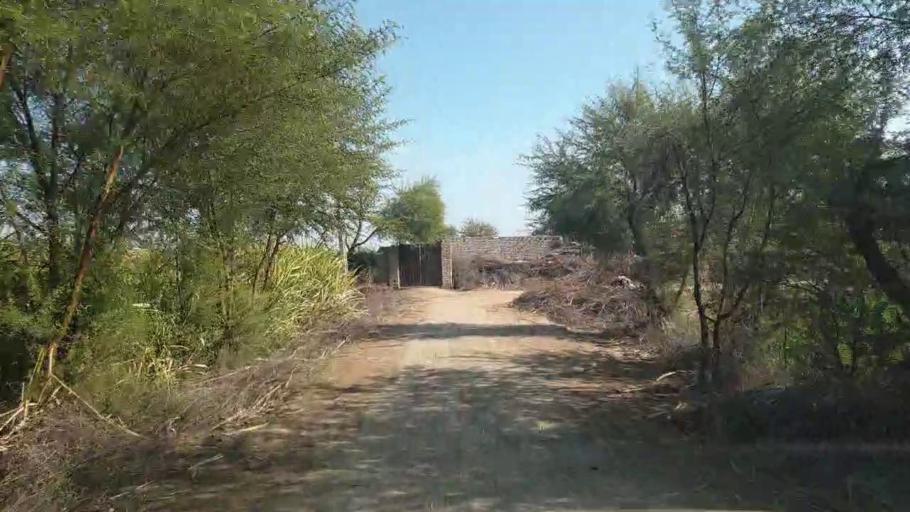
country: PK
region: Sindh
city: Shahdadpur
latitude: 25.9111
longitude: 68.5653
